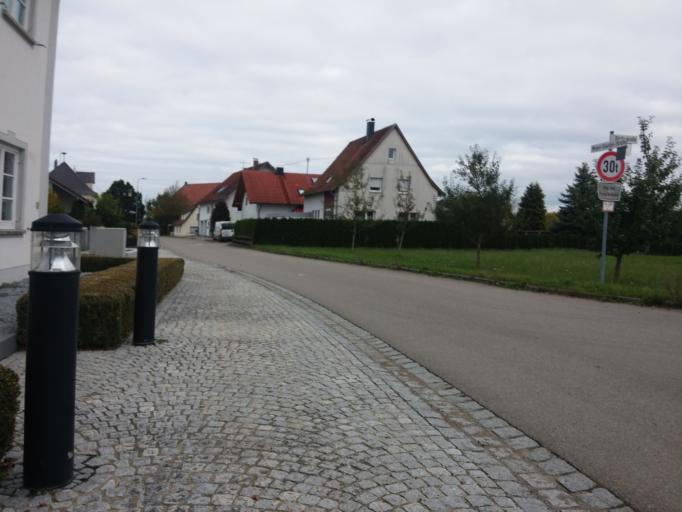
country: DE
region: Baden-Wuerttemberg
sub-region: Tuebingen Region
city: Tannheim
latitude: 47.9721
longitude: 10.0857
